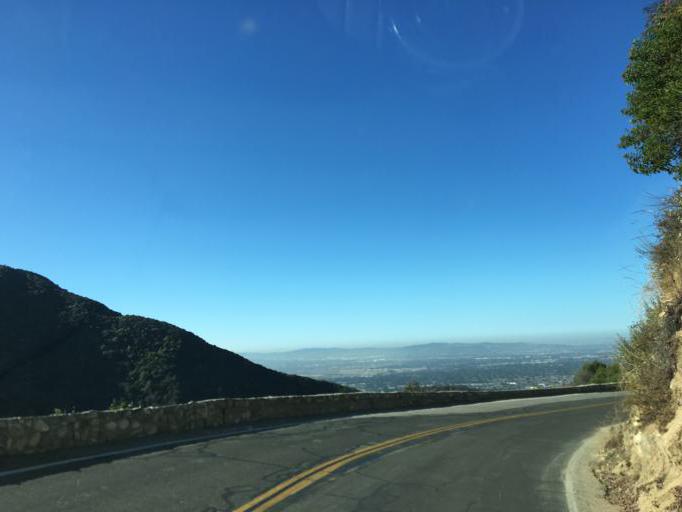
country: US
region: California
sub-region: Los Angeles County
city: Sierra Madre
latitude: 34.1930
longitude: -118.0198
